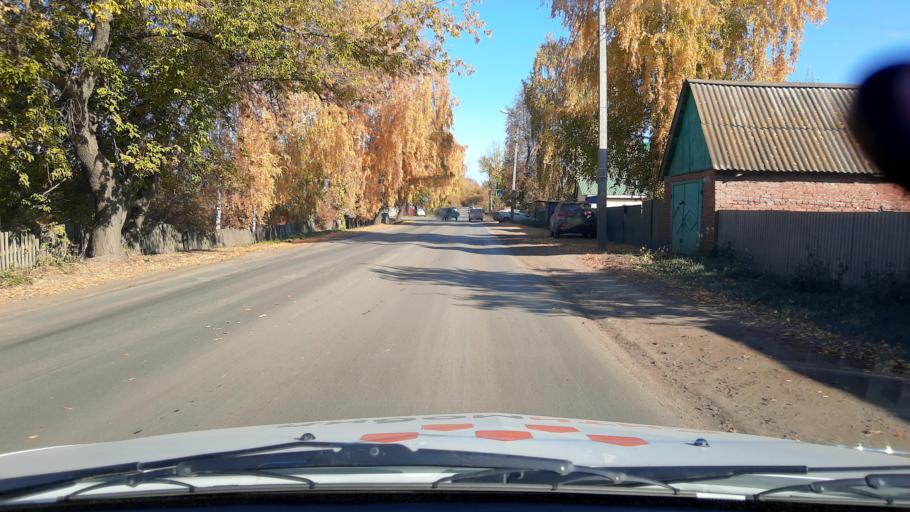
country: RU
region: Bashkortostan
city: Iglino
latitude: 54.7739
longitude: 56.2273
